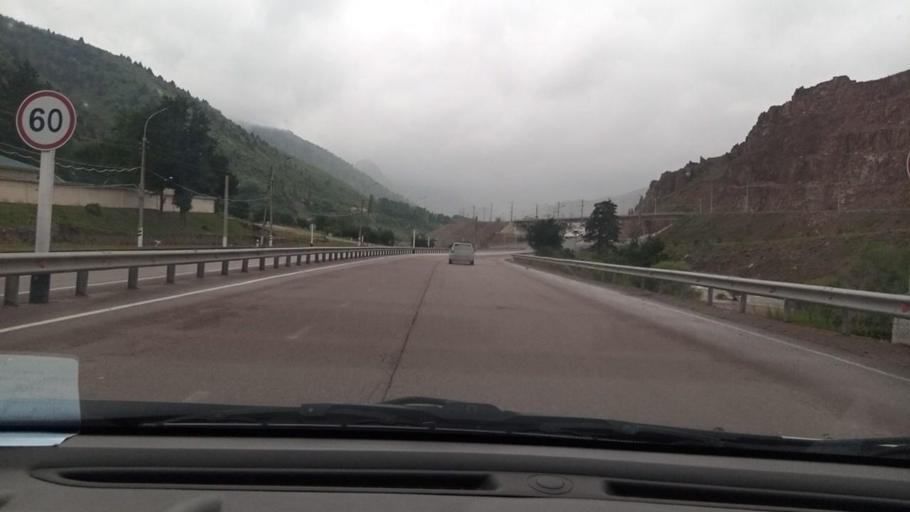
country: UZ
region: Toshkent
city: Angren
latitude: 41.1530
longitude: 70.4409
